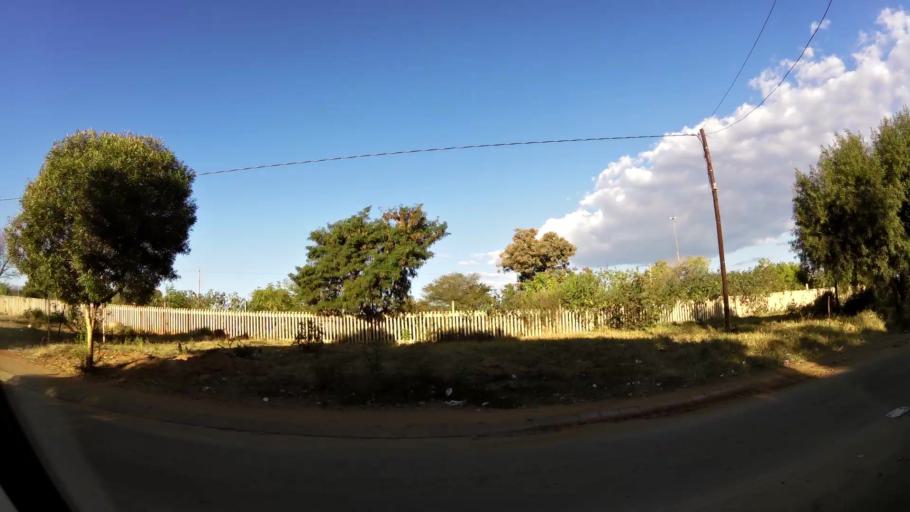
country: ZA
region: Limpopo
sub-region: Waterberg District Municipality
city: Mokopane
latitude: -24.1550
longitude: 28.9853
